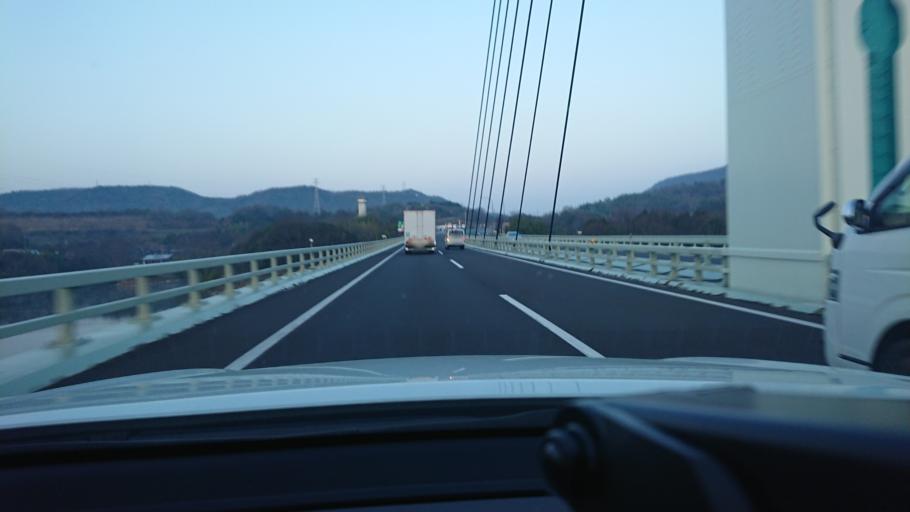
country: JP
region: Kagawa
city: Sakaidecho
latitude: 34.2735
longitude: 133.9277
